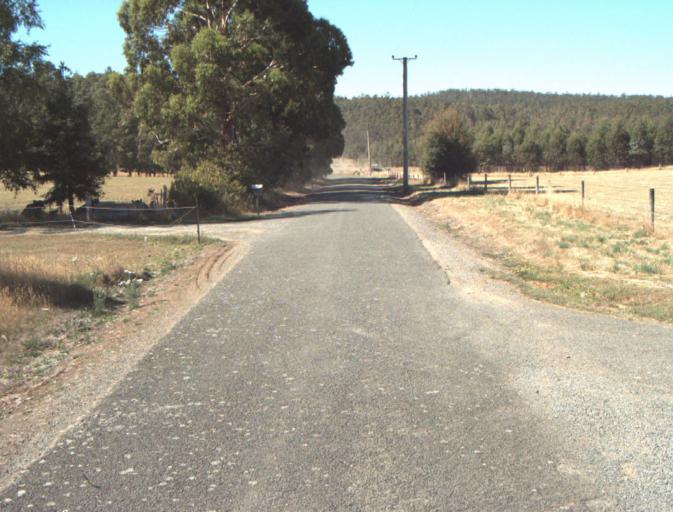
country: AU
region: Tasmania
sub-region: Launceston
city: Newstead
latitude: -41.3193
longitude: 147.3198
